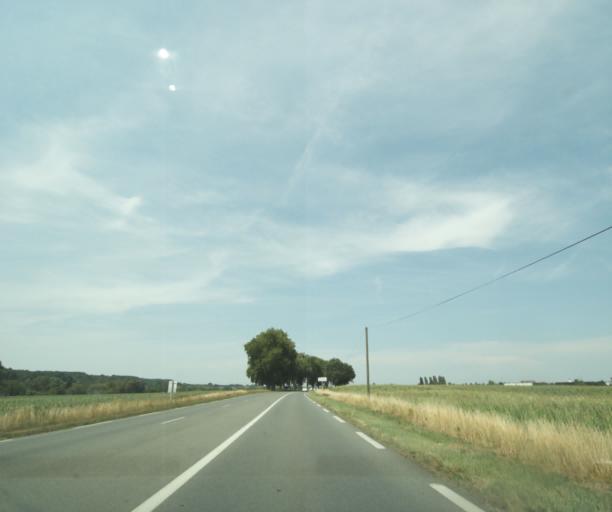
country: FR
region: Poitou-Charentes
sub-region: Departement de la Vienne
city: Antran
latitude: 46.8931
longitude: 0.5694
